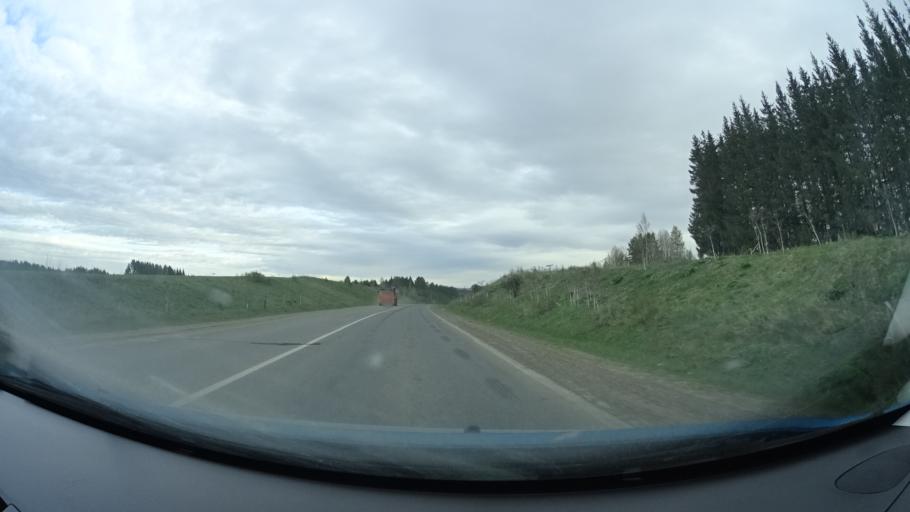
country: RU
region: Perm
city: Osa
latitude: 57.2631
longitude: 55.5750
